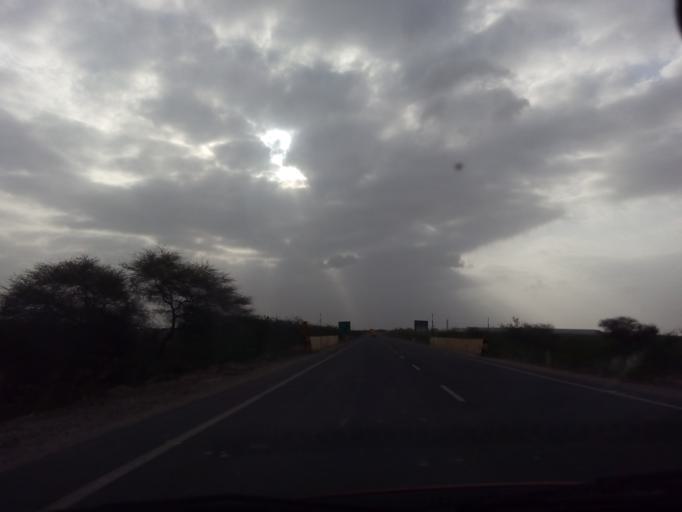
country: IN
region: Gujarat
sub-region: Kachchh
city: Bhuj
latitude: 23.2463
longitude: 69.8337
